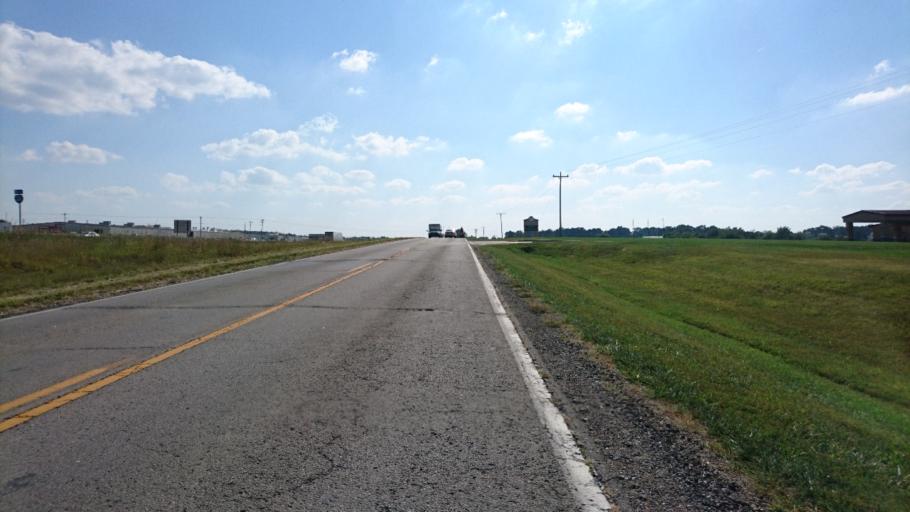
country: US
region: Missouri
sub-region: Laclede County
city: Lebanon
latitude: 37.6435
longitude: -92.6726
